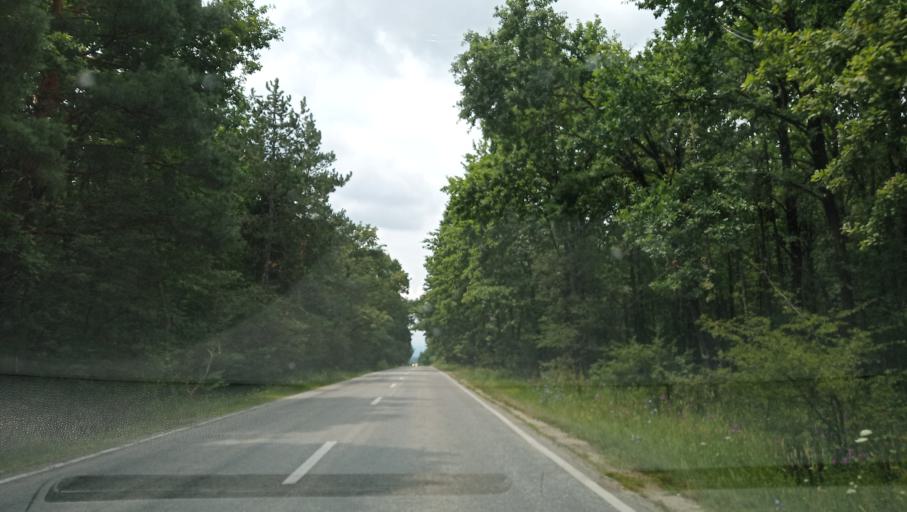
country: RO
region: Gorj
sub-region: Comuna Runcu
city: Balta
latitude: 45.0881
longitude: 23.1032
